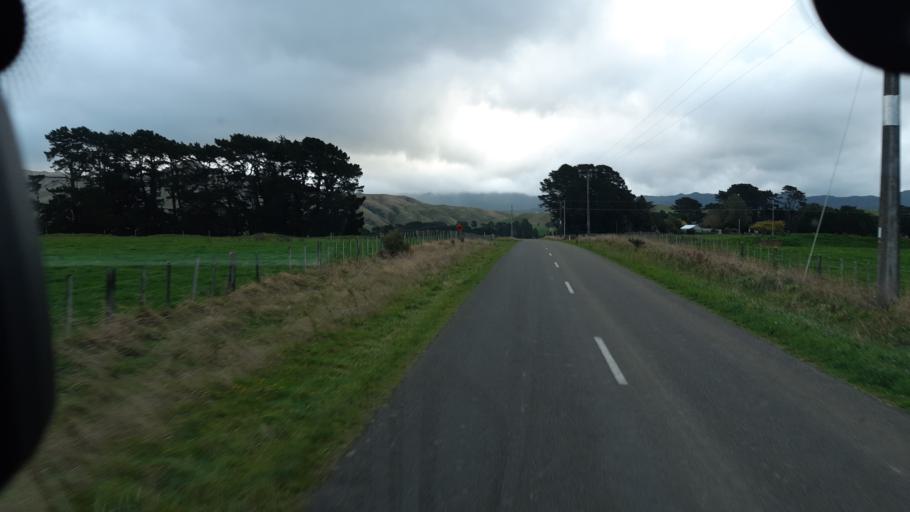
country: NZ
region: Manawatu-Wanganui
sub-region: Palmerston North City
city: Palmerston North
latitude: -40.6440
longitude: 175.6546
